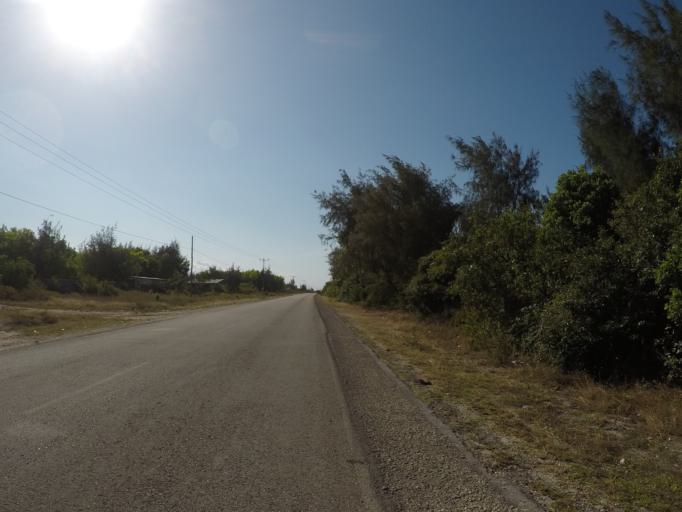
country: TZ
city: Kiwengwa
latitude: -6.1642
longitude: 39.5228
